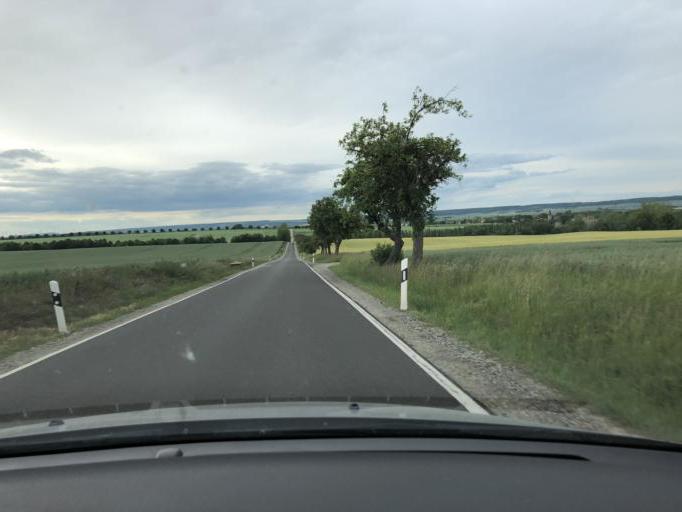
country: DE
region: Thuringia
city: Willerstedt
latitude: 51.0763
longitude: 11.4466
